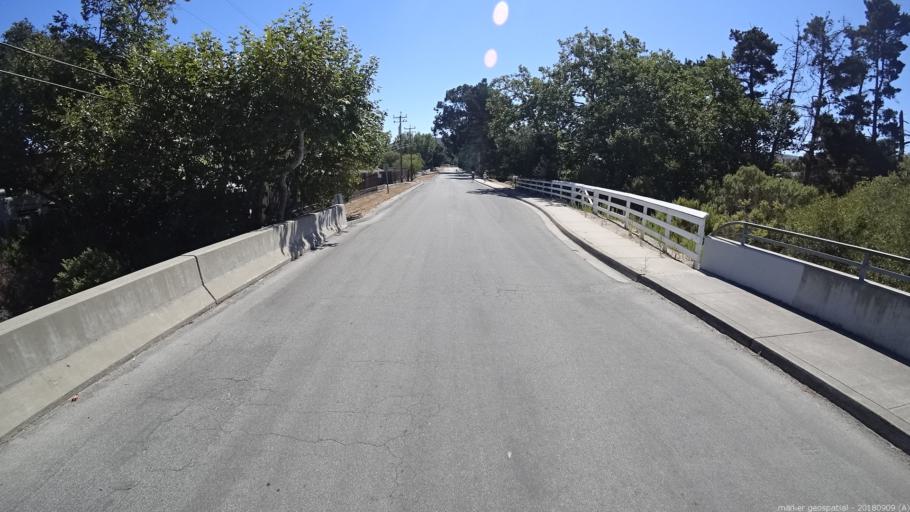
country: US
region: California
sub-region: Monterey County
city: Salinas
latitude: 36.6069
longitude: -121.6980
